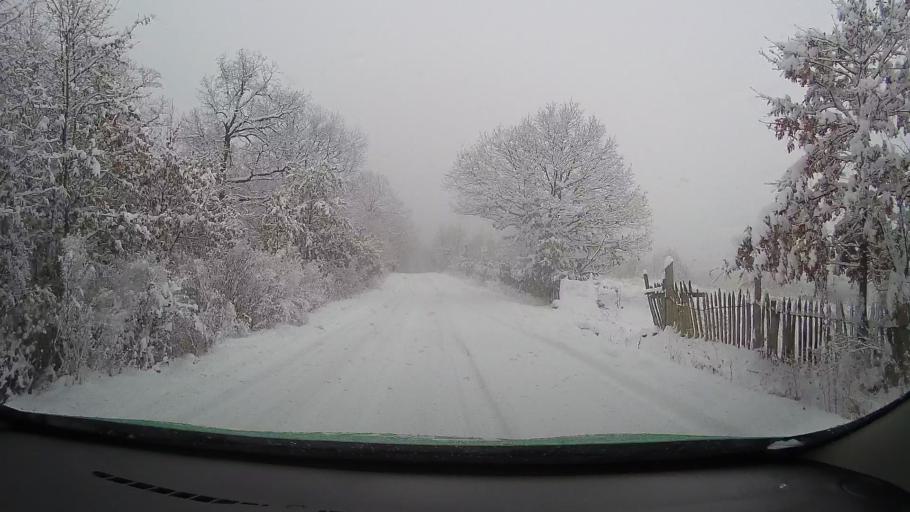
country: RO
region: Hunedoara
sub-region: Comuna Teliucu Inferior
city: Teliucu Inferior
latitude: 45.6906
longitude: 22.8939
